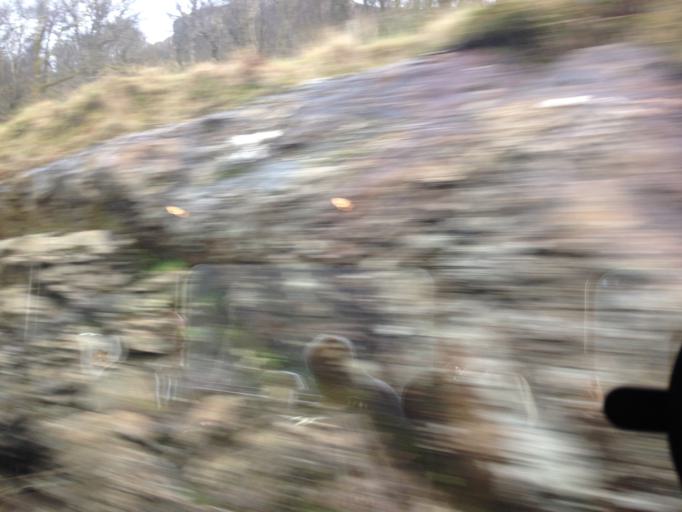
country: GB
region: Scotland
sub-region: Argyll and Bute
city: Garelochhead
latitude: 56.1692
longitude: -4.7808
